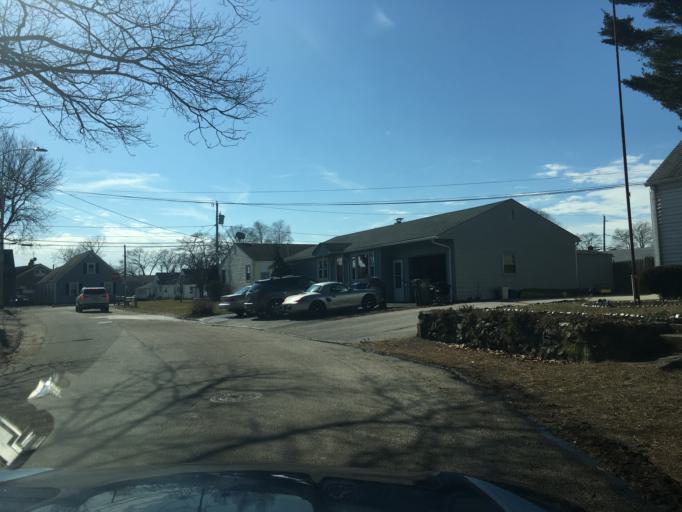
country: US
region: Rhode Island
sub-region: Providence County
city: Cranston
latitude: 41.7852
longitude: -71.4419
